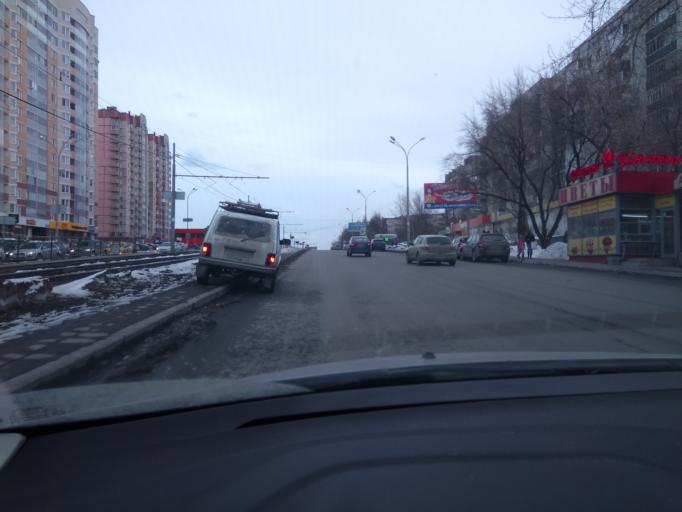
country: RU
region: Sverdlovsk
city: Yekaterinburg
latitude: 56.8540
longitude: 60.6364
